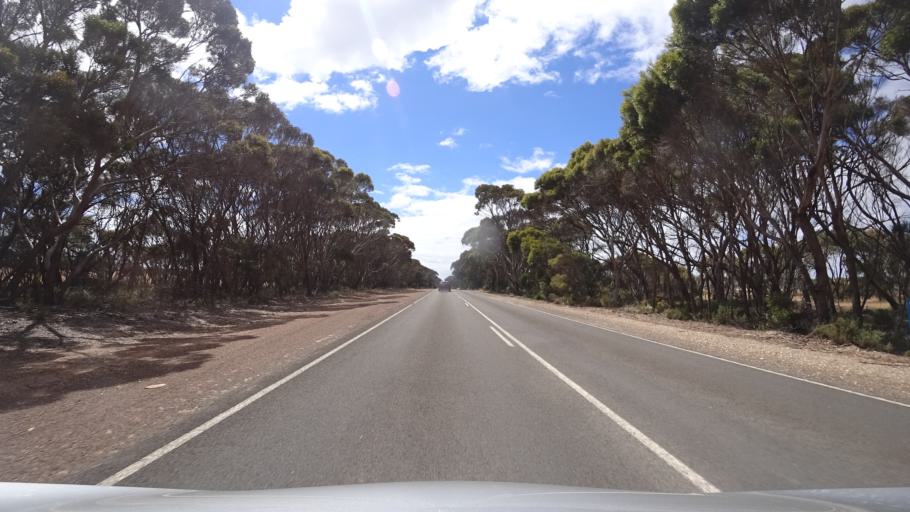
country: AU
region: South Australia
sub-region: Kangaroo Island
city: Kingscote
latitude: -35.6564
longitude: 137.5746
